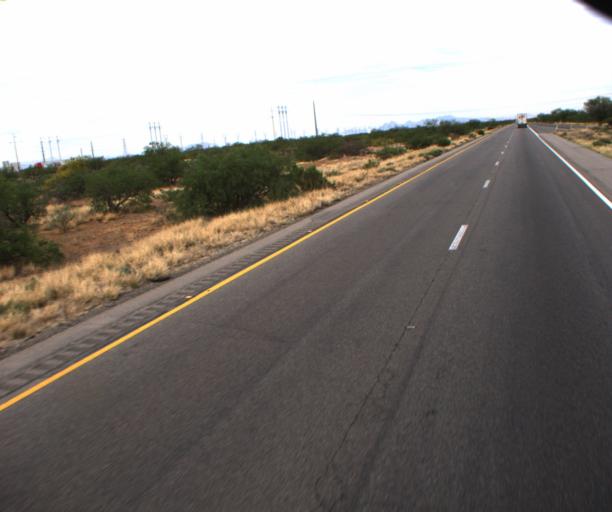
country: US
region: Arizona
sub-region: Pima County
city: Vail
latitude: 32.0294
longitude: -110.7217
